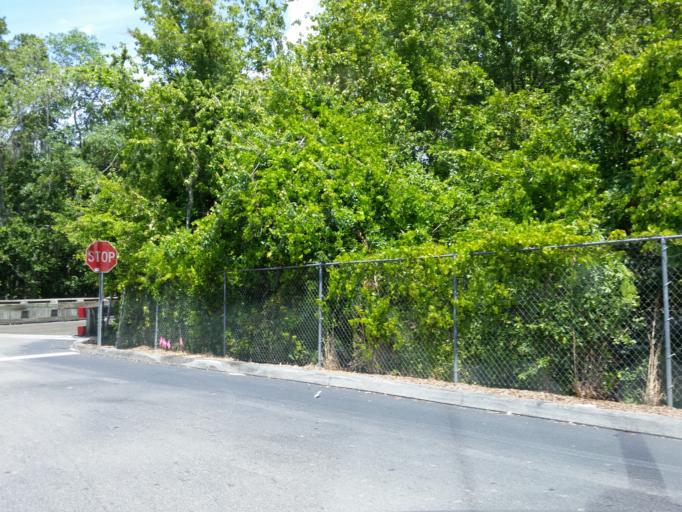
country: US
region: Florida
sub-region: Hillsborough County
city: Plant City
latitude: 28.0239
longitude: -82.1495
